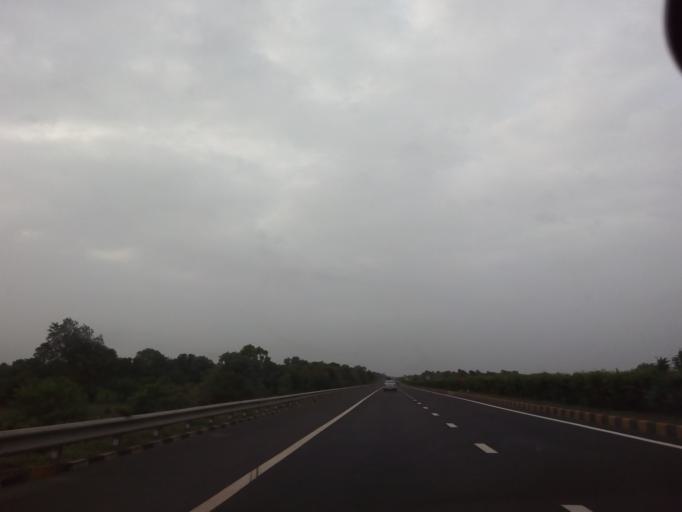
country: IN
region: Gujarat
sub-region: Kheda
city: Chaklasi
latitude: 22.6668
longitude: 72.9174
